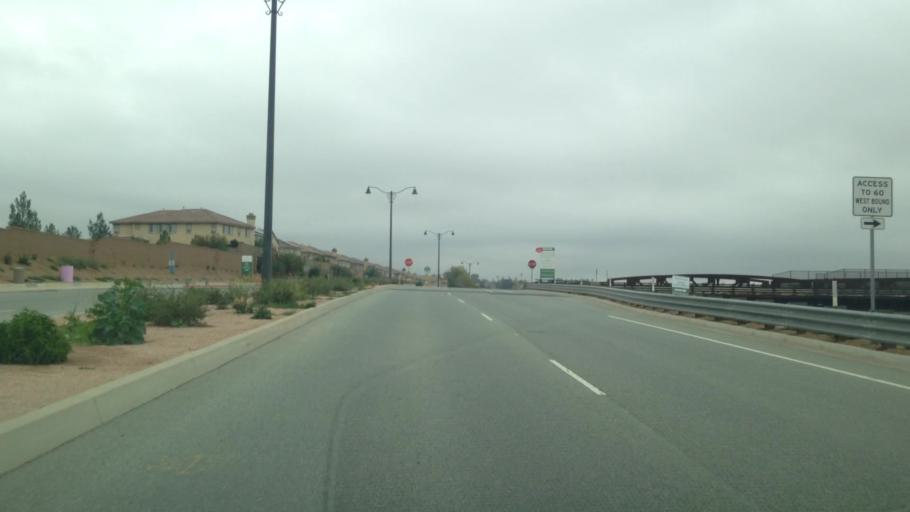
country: US
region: California
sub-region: Riverside County
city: Beaumont
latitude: 33.9442
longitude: -117.0183
